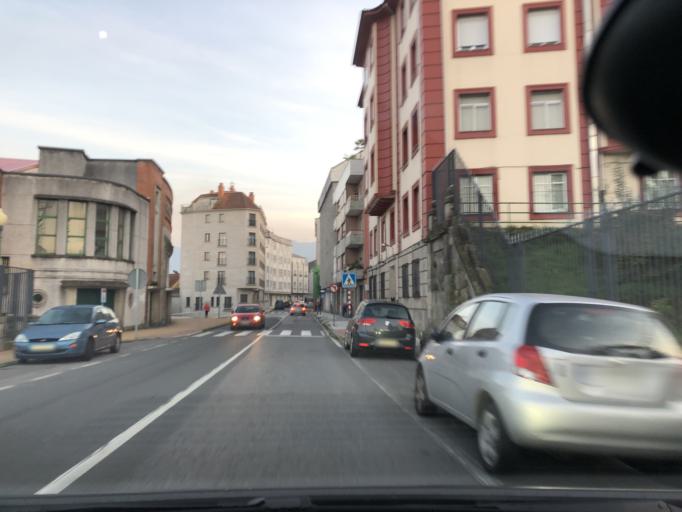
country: ES
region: Galicia
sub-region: Provincia de Pontevedra
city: Marin
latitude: 42.3937
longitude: -8.7068
